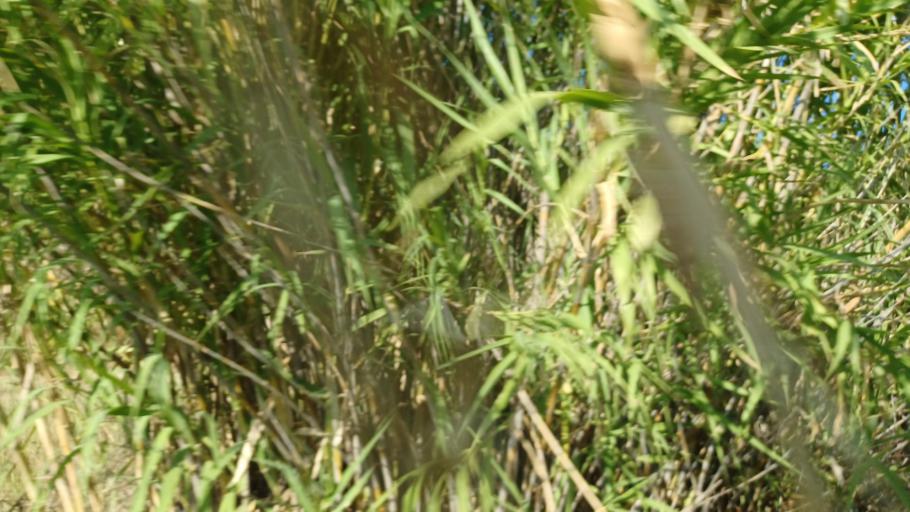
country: CY
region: Pafos
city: Mesogi
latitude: 34.8804
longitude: 32.5207
